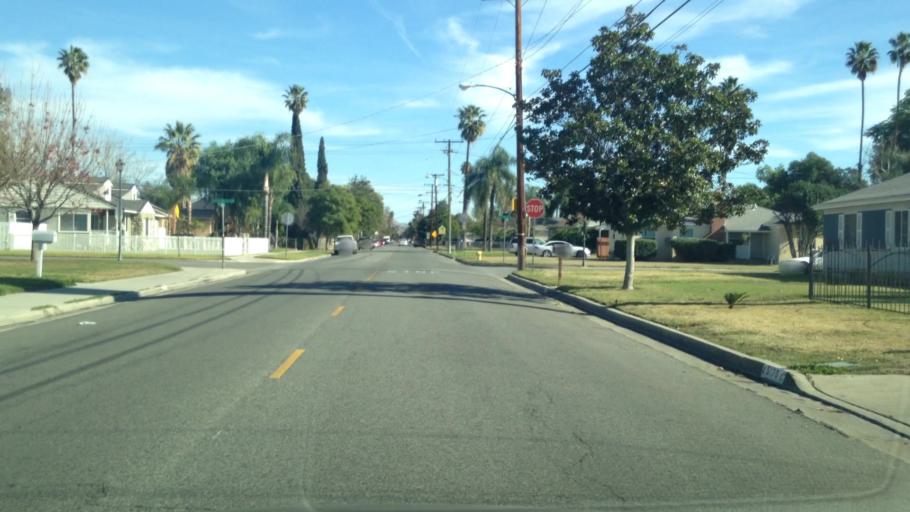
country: US
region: California
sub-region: Riverside County
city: Riverside
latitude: 33.9497
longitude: -117.4159
